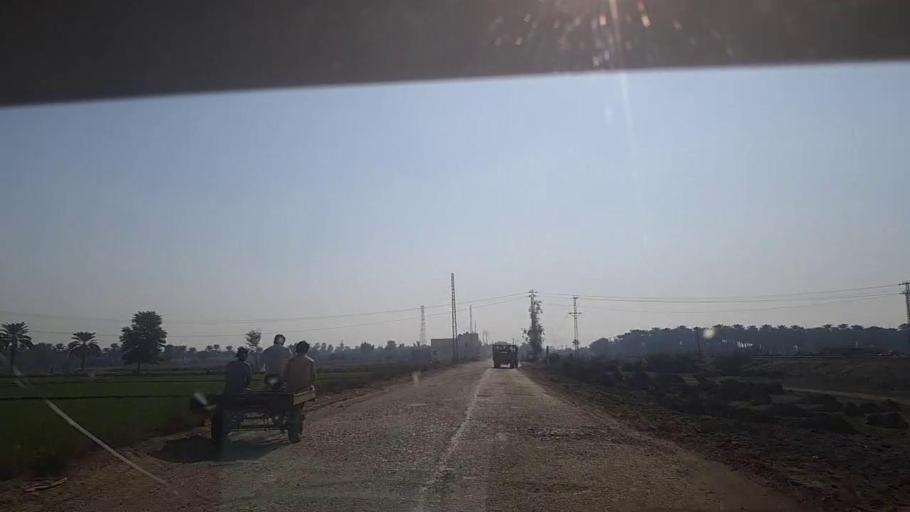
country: PK
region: Sindh
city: Gambat
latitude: 27.3484
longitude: 68.5493
